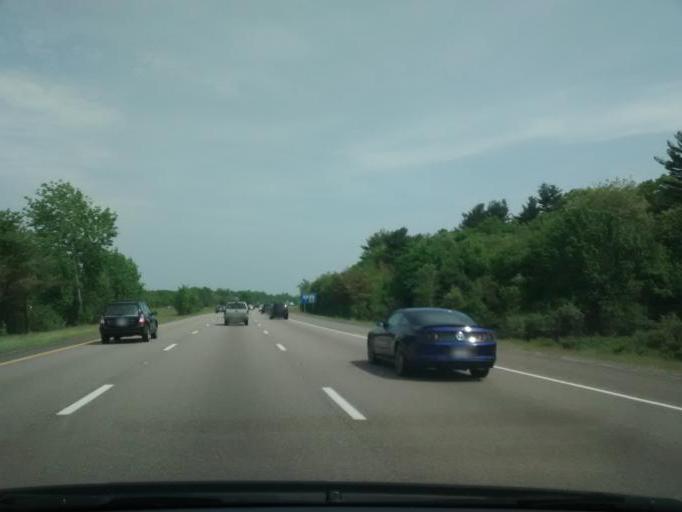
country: US
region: Massachusetts
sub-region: Bristol County
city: Mansfield Center
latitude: 42.0235
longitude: -71.2508
